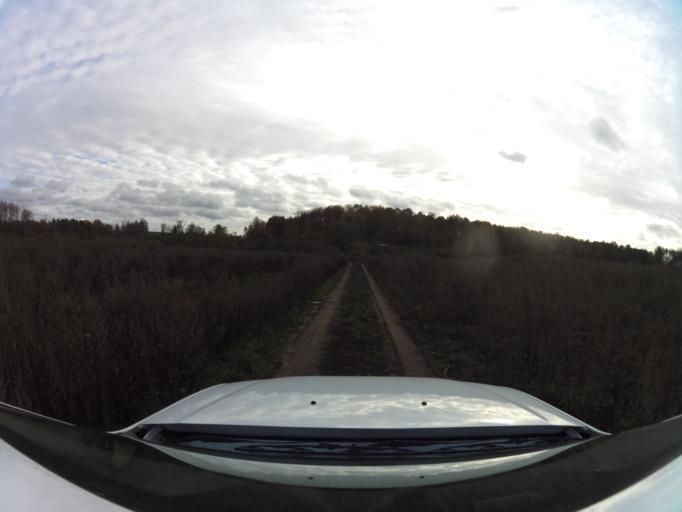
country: PL
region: West Pomeranian Voivodeship
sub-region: Powiat gryficki
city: Gryfice
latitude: 53.8387
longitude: 15.1125
